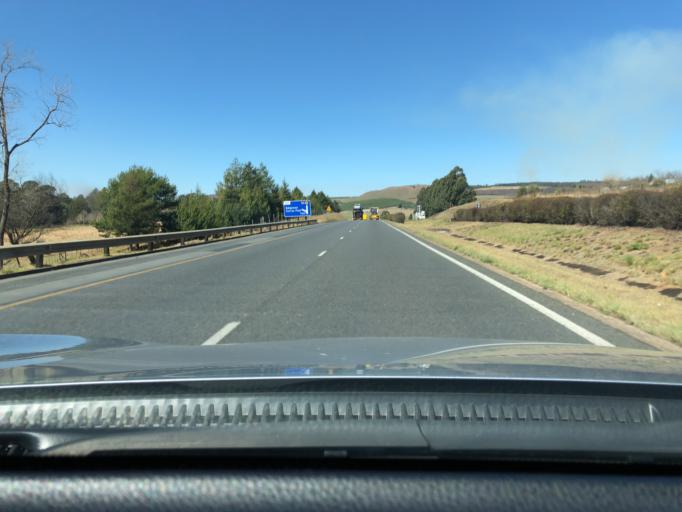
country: ZA
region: KwaZulu-Natal
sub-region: uMgungundlovu District Municipality
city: Mooirivier
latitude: -29.3492
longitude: 30.0863
